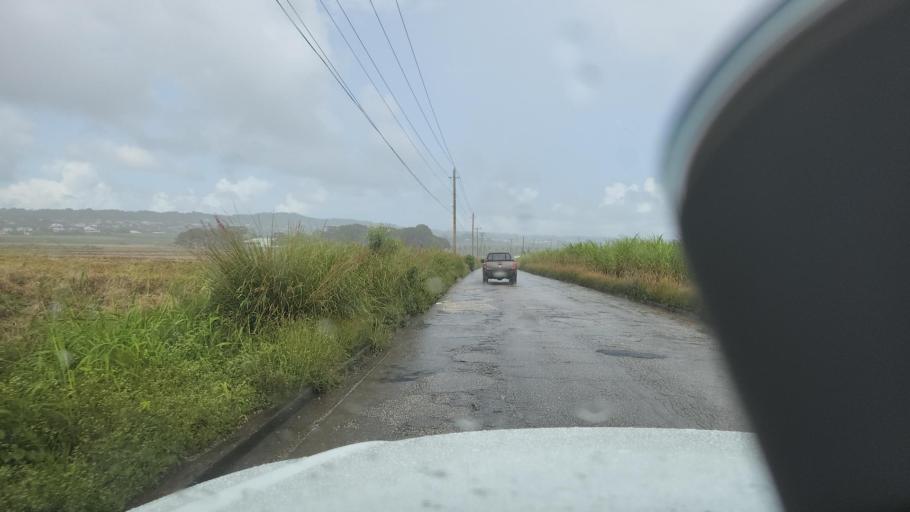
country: BB
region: Saint Michael
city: Bridgetown
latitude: 13.1189
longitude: -59.5709
